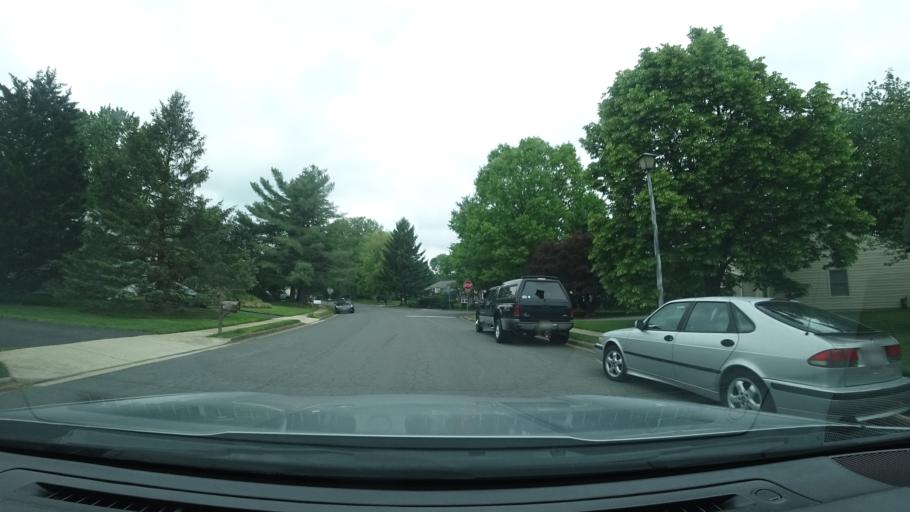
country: US
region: Virginia
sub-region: Fairfax County
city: Oak Hill
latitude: 38.9359
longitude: -77.3829
